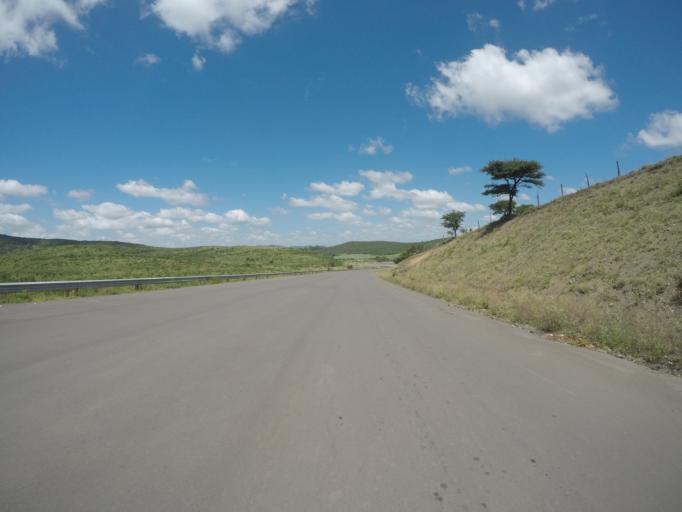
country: ZA
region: KwaZulu-Natal
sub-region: uThungulu District Municipality
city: Empangeni
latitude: -28.6144
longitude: 31.7534
